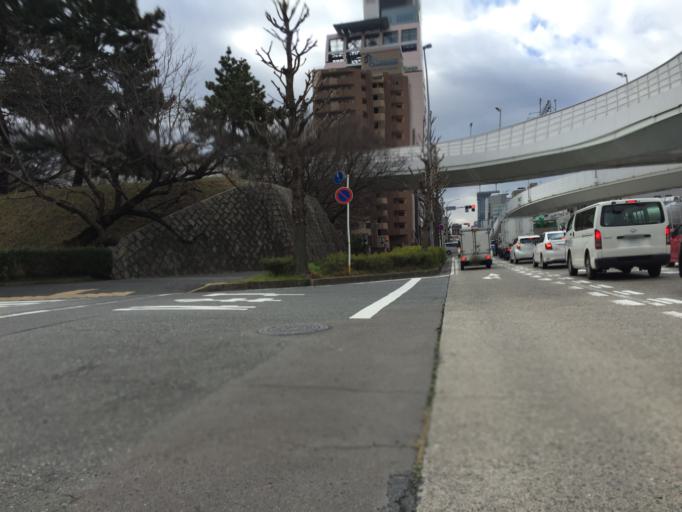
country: JP
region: Aichi
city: Nagoya-shi
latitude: 35.1786
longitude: 136.8967
